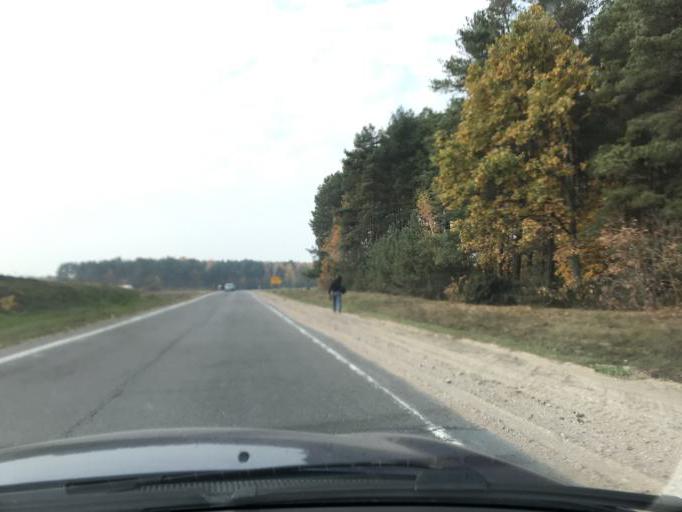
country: BY
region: Grodnenskaya
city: Lida
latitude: 53.8310
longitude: 25.3552
